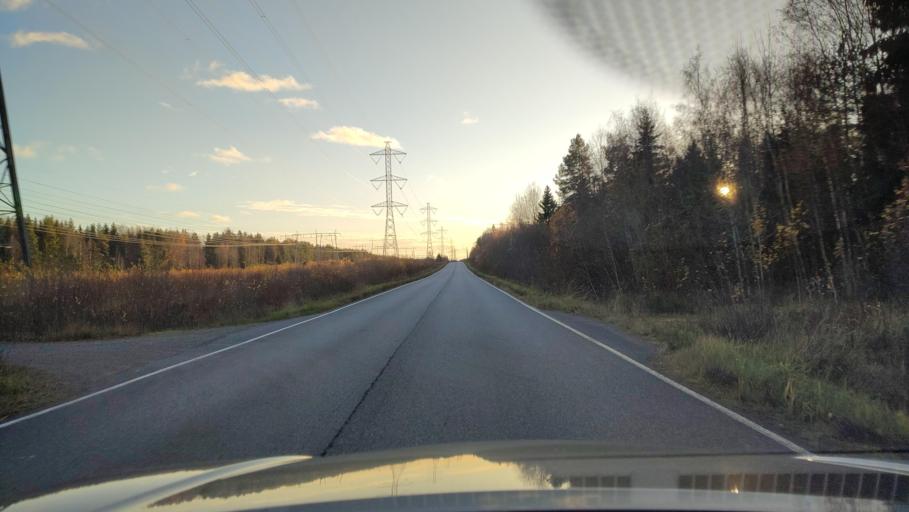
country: FI
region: Ostrobothnia
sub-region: Sydosterbotten
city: Kristinestad
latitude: 62.2936
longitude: 21.3678
